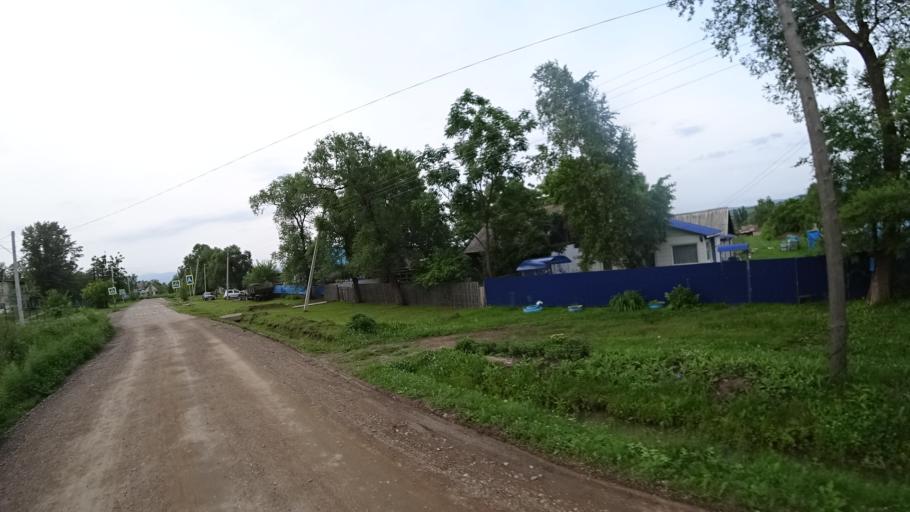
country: RU
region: Primorskiy
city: Novosysoyevka
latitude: 44.2382
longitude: 133.3644
